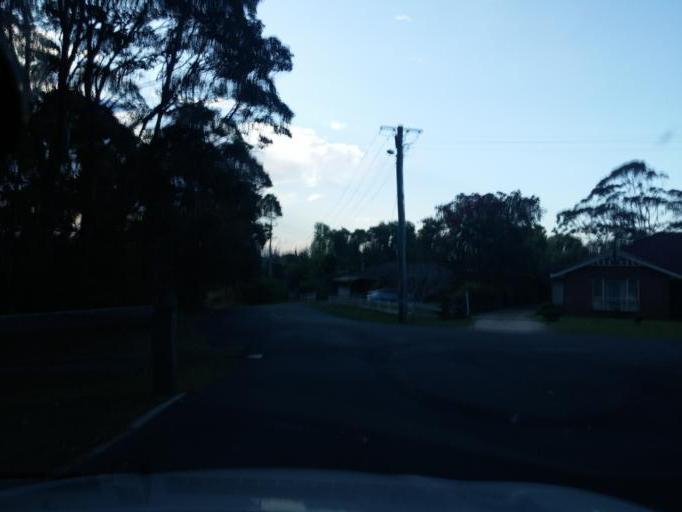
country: AU
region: New South Wales
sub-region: Port Macquarie-Hastings
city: Port Macquarie
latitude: -31.4412
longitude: 152.9186
